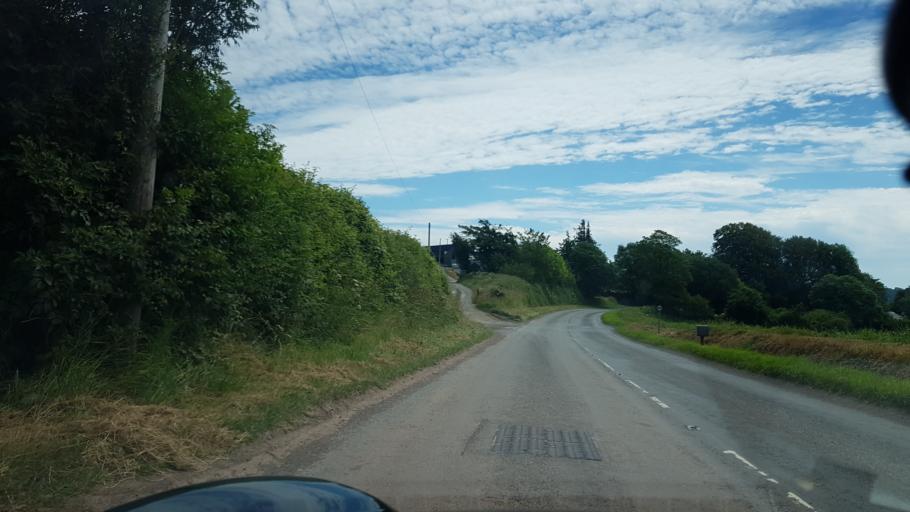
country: GB
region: Wales
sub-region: Carmarthenshire
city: Saint Clears
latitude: 51.7829
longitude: -4.4721
